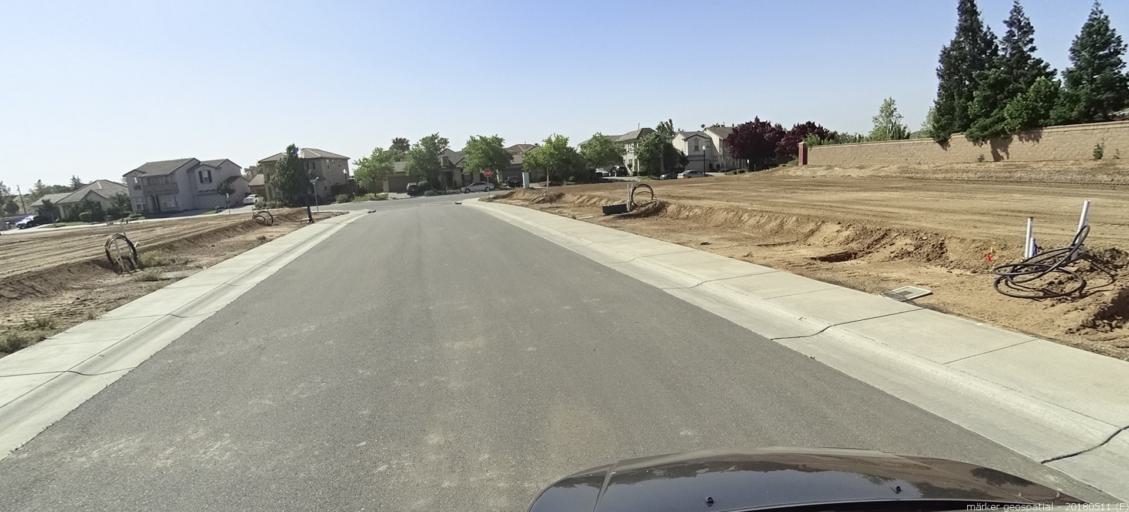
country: US
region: California
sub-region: Yolo County
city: West Sacramento
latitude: 38.6678
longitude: -121.5437
